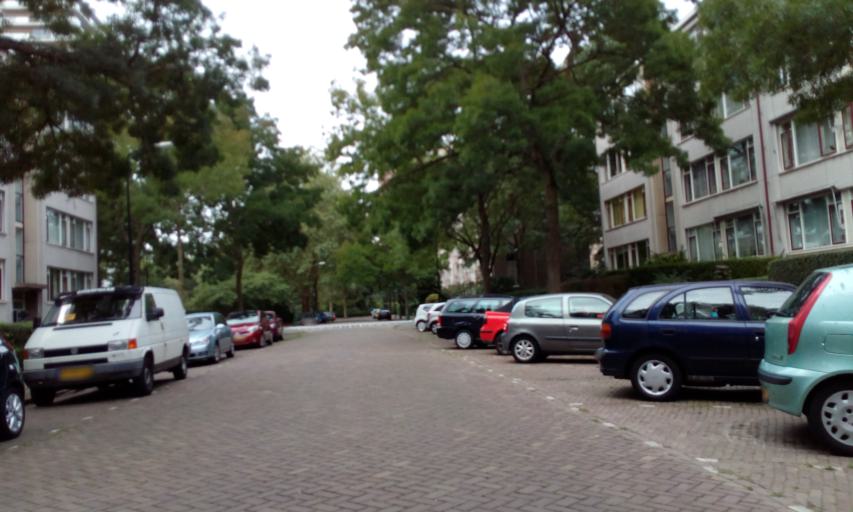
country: NL
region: South Holland
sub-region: Gemeente Rijswijk
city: Rijswijk
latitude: 52.0314
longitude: 4.3231
